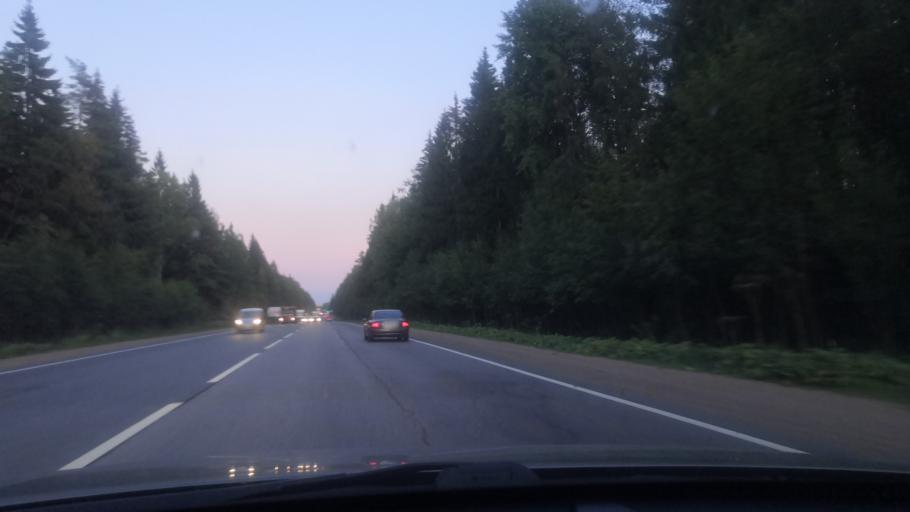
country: RU
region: St.-Petersburg
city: Pesochnyy
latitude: 60.1868
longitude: 30.1089
